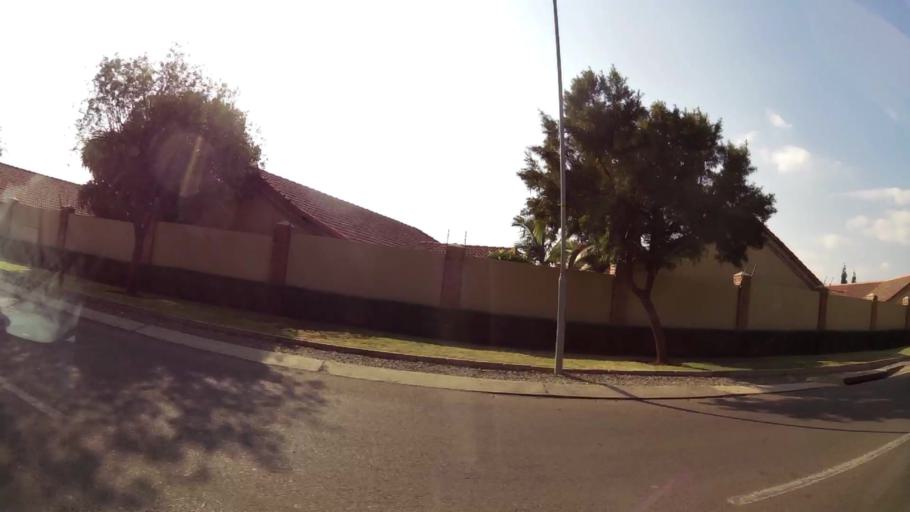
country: ZA
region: Gauteng
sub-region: City of Tshwane Metropolitan Municipality
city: Pretoria
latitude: -25.7692
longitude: 28.3434
